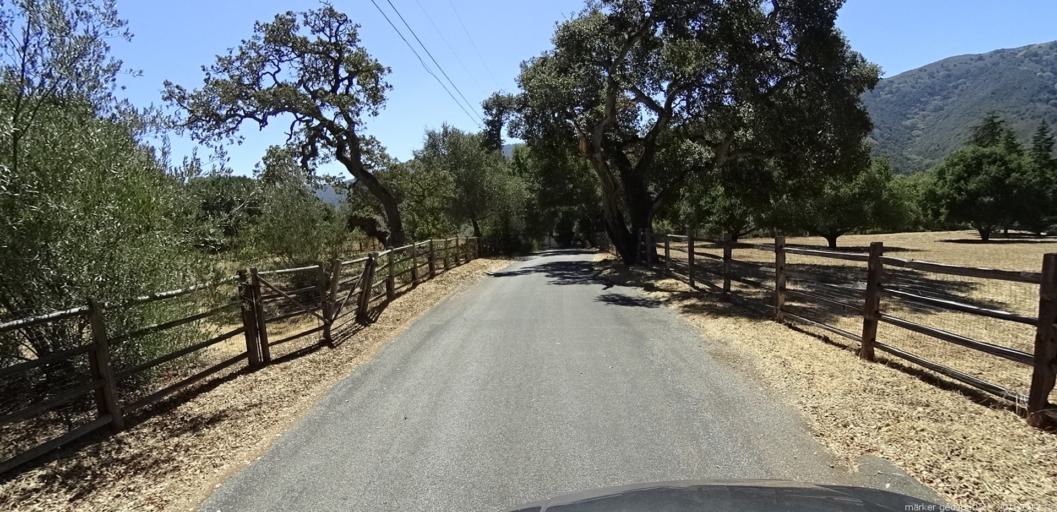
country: US
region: California
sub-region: Monterey County
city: Carmel Valley Village
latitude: 36.5081
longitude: -121.7579
